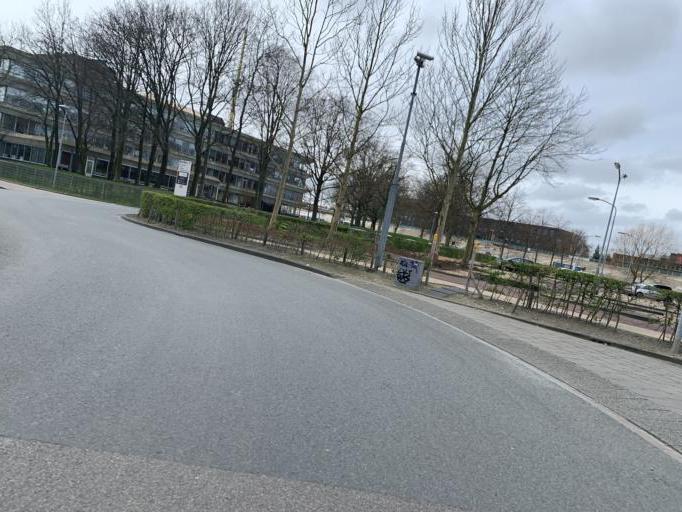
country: NL
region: Groningen
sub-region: Gemeente Groningen
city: Oosterpark
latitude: 53.2095
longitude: 6.5882
